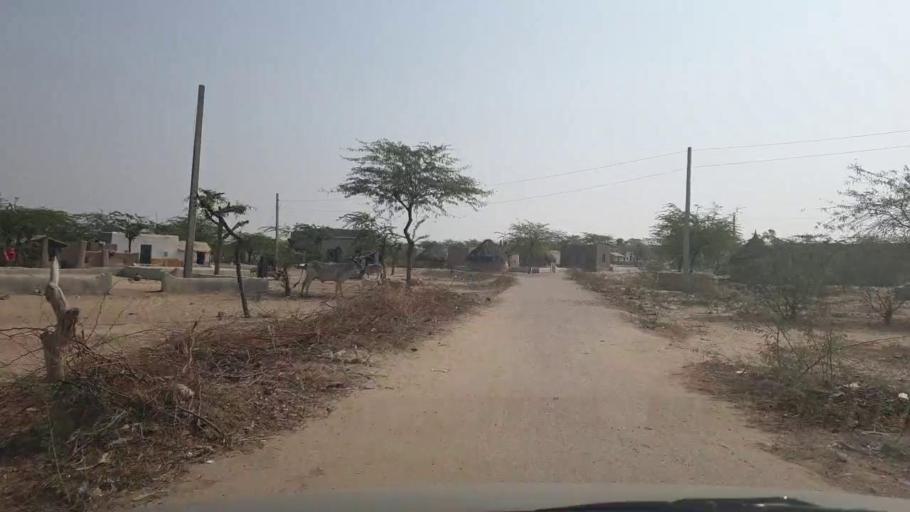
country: PK
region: Sindh
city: Umarkot
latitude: 25.4327
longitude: 69.7491
